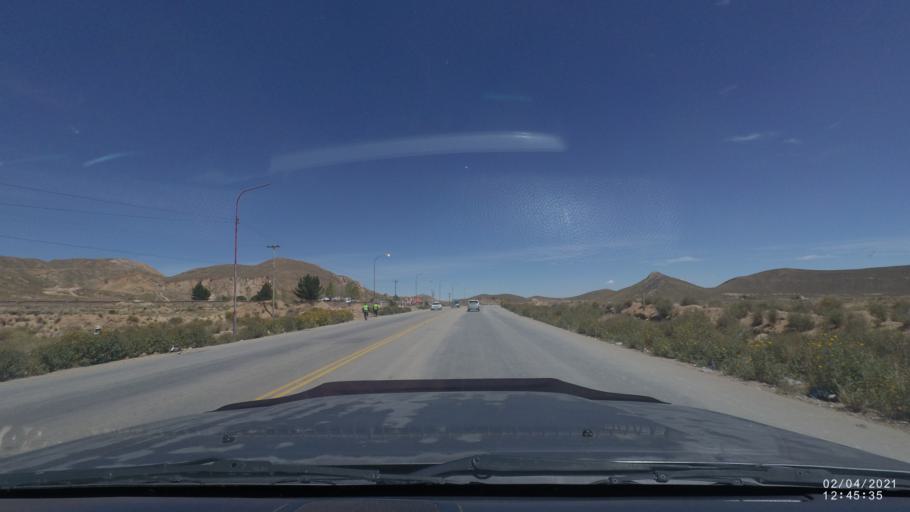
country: BO
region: Oruro
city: Oruro
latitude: -17.9368
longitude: -67.1347
